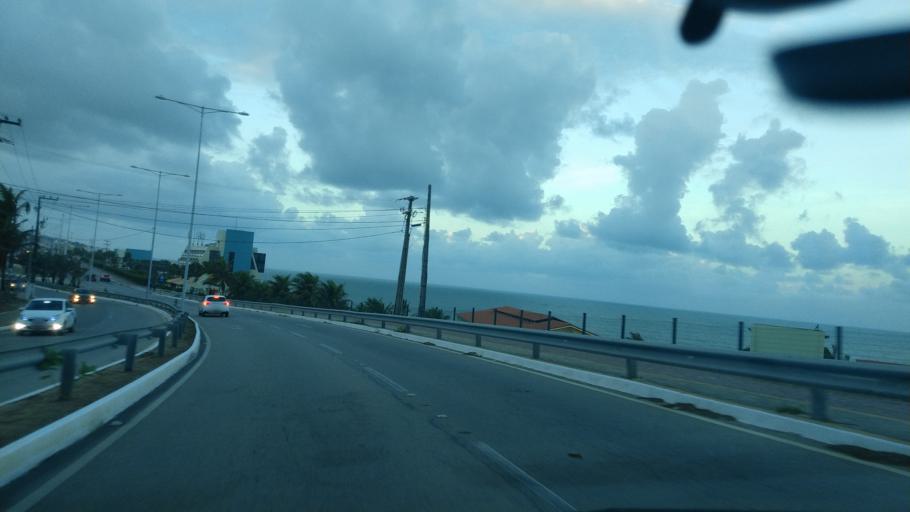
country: BR
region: Rio Grande do Norte
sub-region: Natal
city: Natal
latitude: -5.8652
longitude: -35.1808
